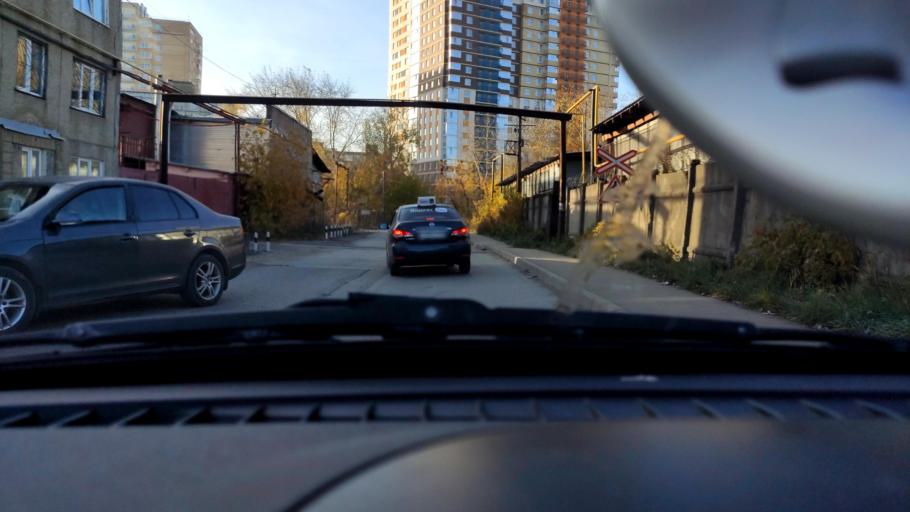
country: RU
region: Perm
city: Kondratovo
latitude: 58.0014
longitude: 56.1513
